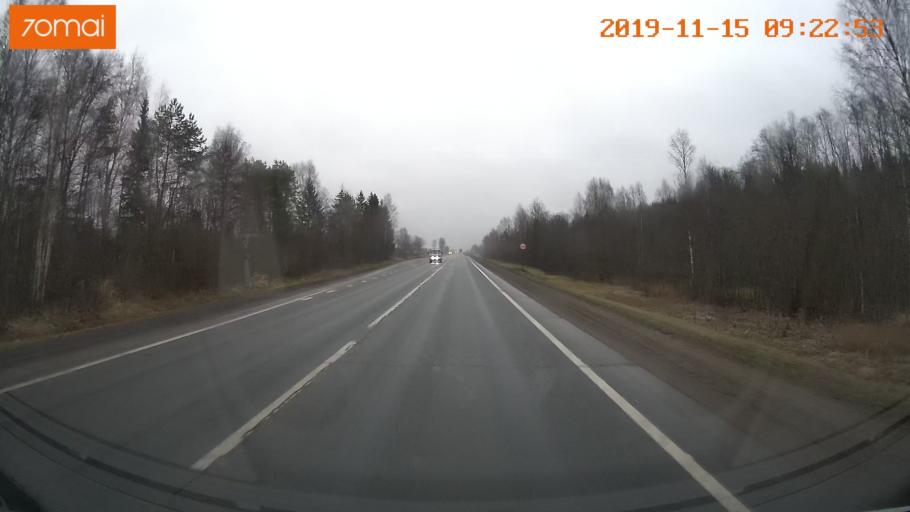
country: RU
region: Vologda
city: Tonshalovo
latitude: 59.2992
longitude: 38.0996
